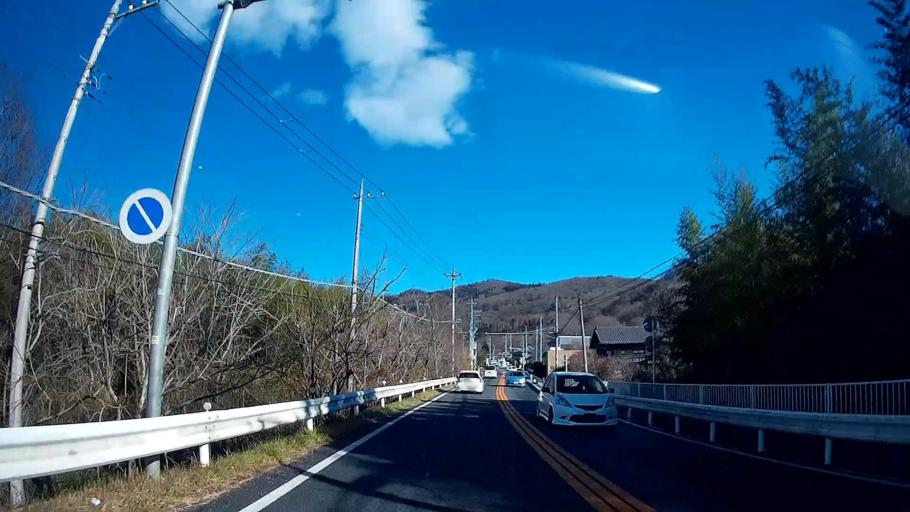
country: JP
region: Saitama
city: Chichibu
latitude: 36.0347
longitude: 139.1080
